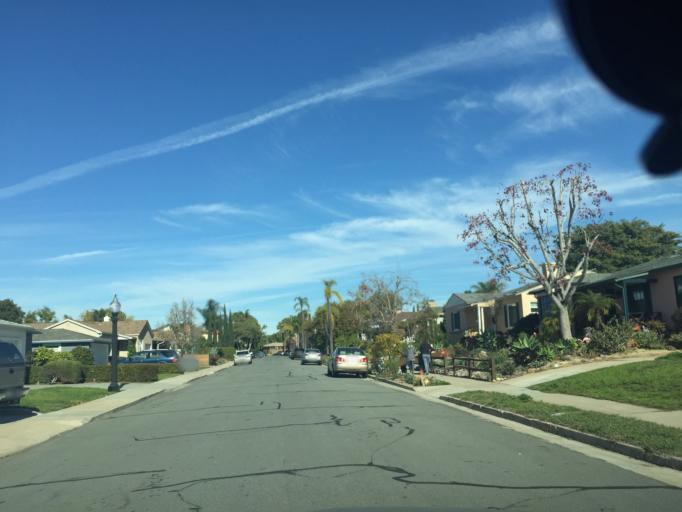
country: US
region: California
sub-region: San Diego County
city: Lemon Grove
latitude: 32.7621
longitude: -117.0953
